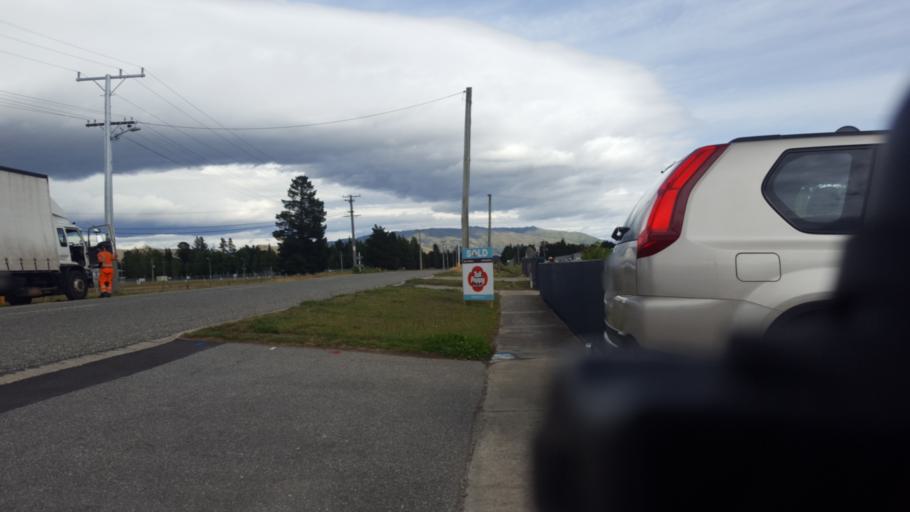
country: NZ
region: Otago
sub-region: Queenstown-Lakes District
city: Wanaka
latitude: -45.2412
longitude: 169.3906
